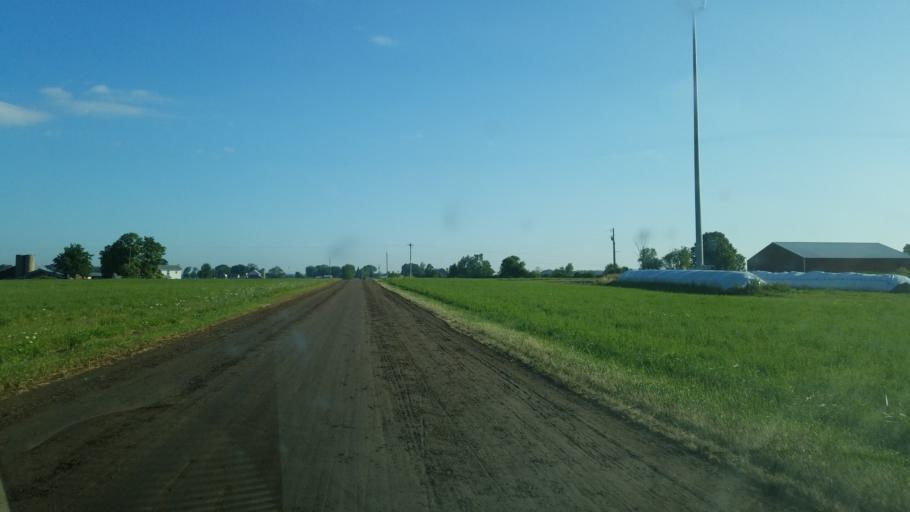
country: US
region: Michigan
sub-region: Mecosta County
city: Canadian Lakes
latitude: 43.5669
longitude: -85.3634
